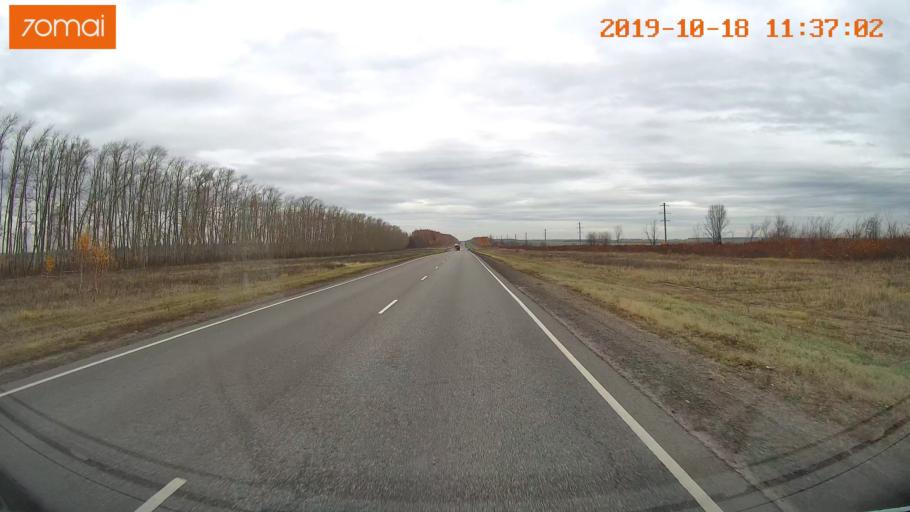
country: RU
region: Rjazan
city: Oktyabr'skiy
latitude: 54.1472
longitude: 38.8205
